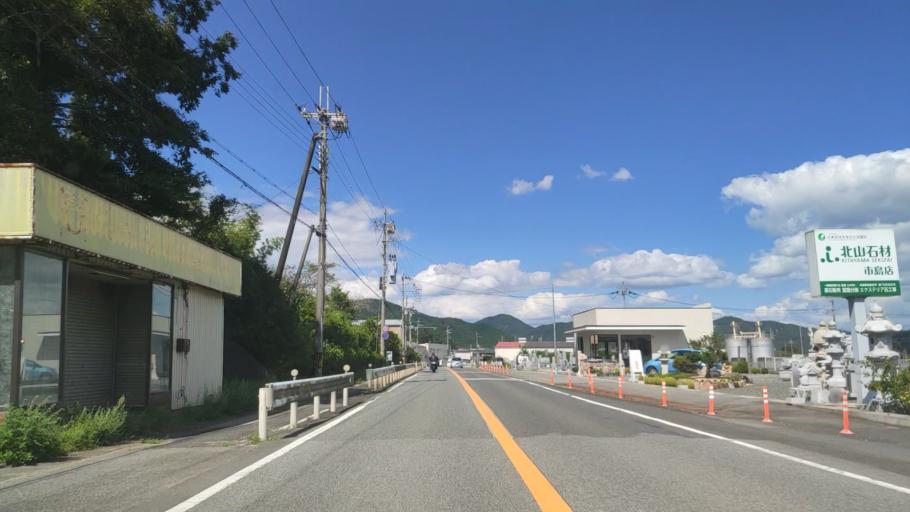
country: JP
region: Kyoto
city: Fukuchiyama
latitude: 35.2178
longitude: 135.1317
